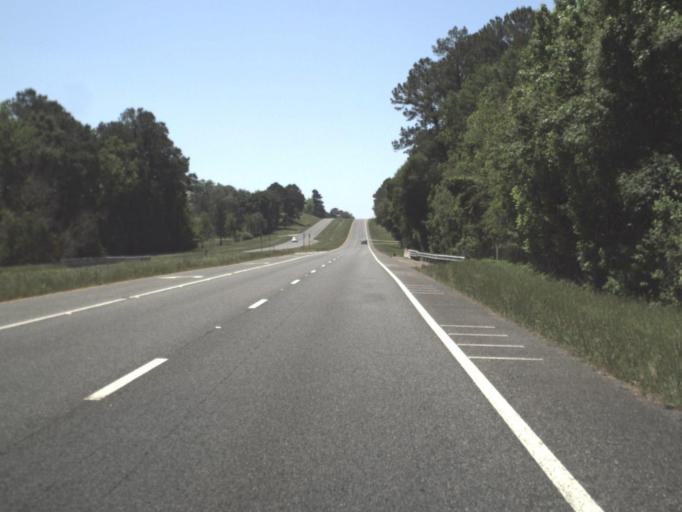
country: US
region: Florida
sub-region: Jefferson County
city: Monticello
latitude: 30.6260
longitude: -83.8728
